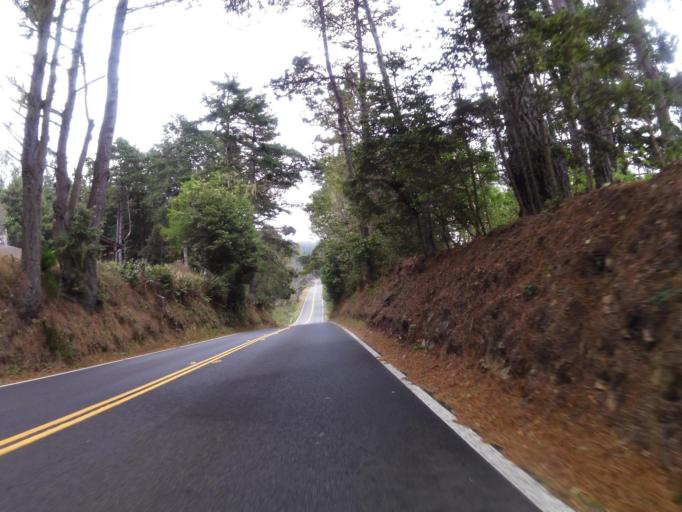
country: US
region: California
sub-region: Sonoma County
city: Sea Ranch
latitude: 38.5416
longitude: -123.2878
